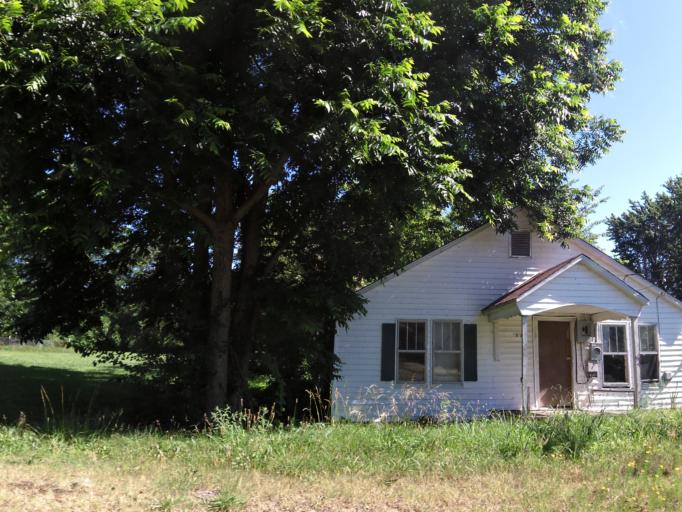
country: US
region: Arkansas
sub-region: Clay County
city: Piggott
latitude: 36.3799
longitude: -90.1934
